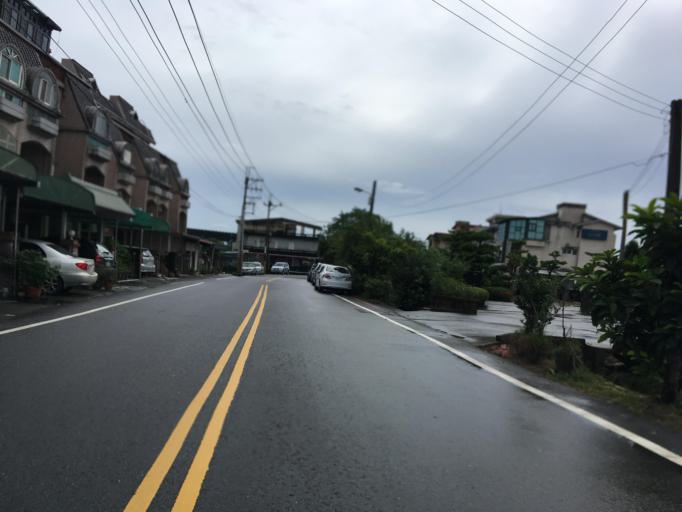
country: TW
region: Taiwan
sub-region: Yilan
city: Yilan
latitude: 24.6644
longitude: 121.7962
